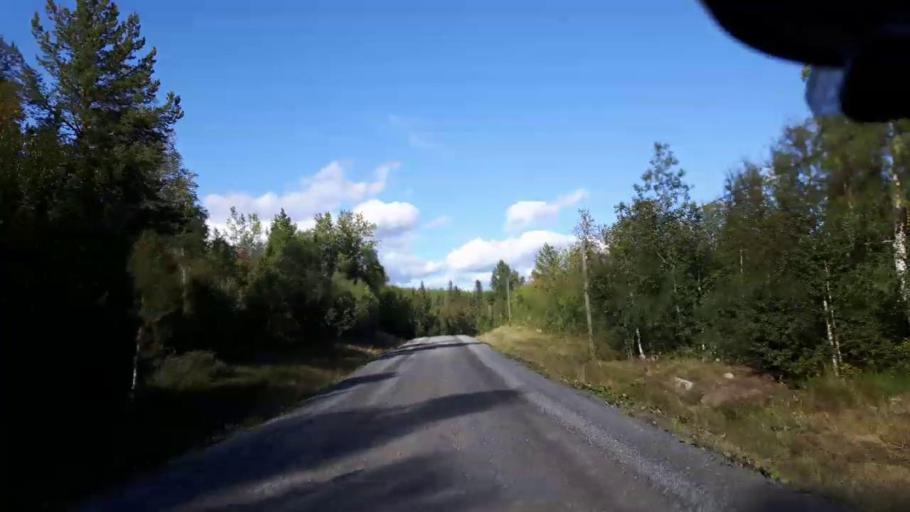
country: SE
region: Jaemtland
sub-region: Ragunda Kommun
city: Hammarstrand
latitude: 63.4384
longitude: 16.1909
